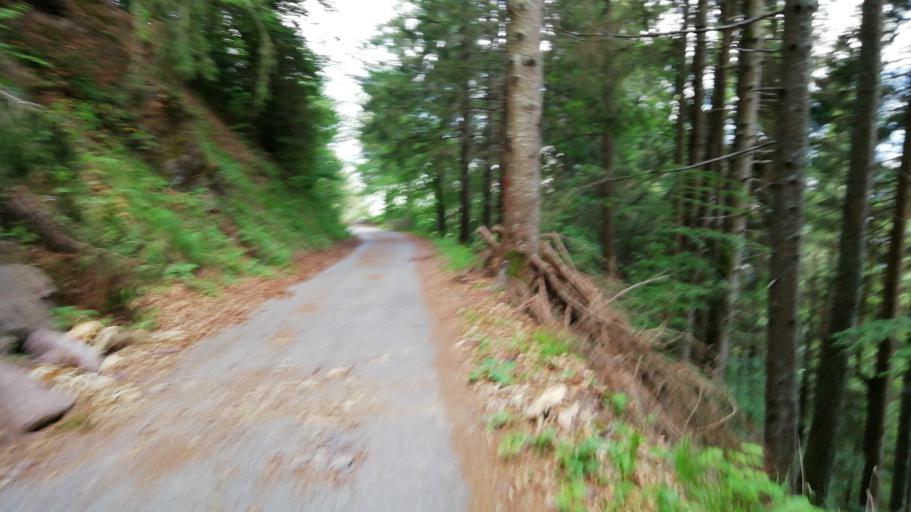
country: IT
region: Veneto
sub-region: Provincia di Belluno
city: Valle di Cadore
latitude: 46.4234
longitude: 12.3228
